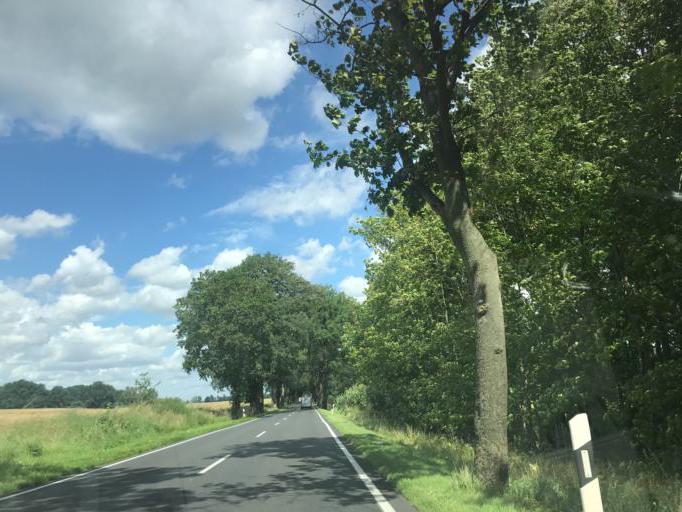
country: DE
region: Brandenburg
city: Gransee
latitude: 52.9184
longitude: 13.1574
